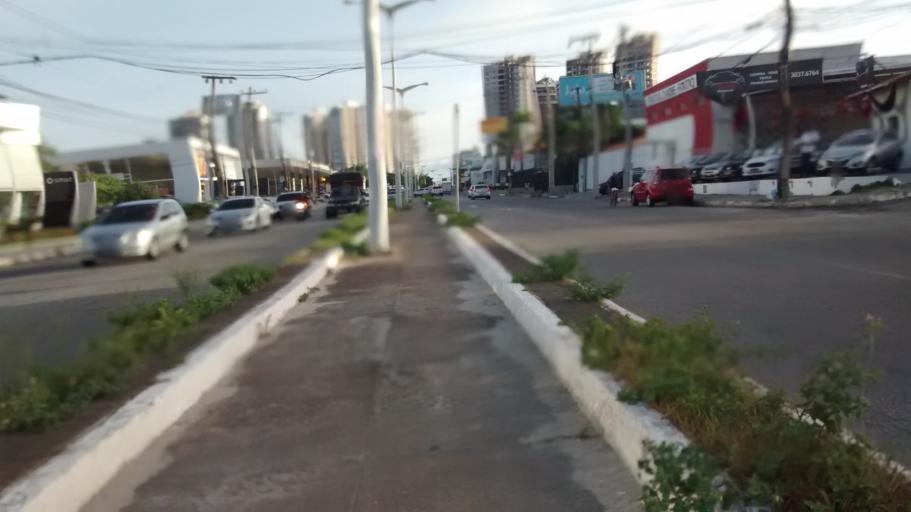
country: BR
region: Ceara
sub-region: Fortaleza
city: Fortaleza
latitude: -3.7606
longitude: -38.4927
